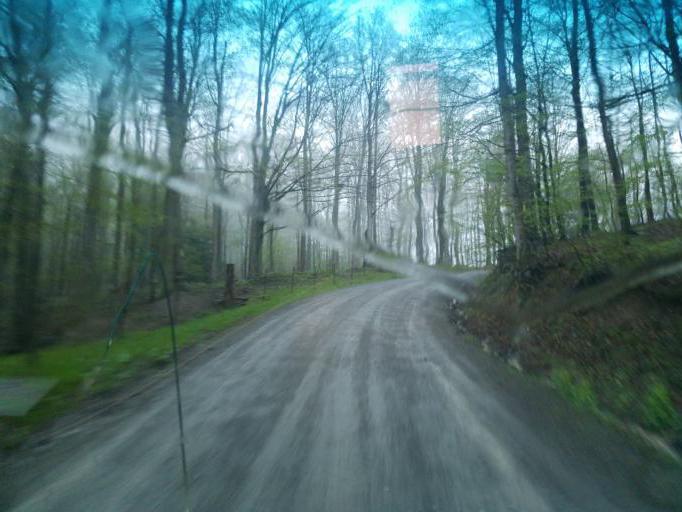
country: US
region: Pennsylvania
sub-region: Tioga County
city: Westfield
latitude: 41.9348
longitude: -77.6939
